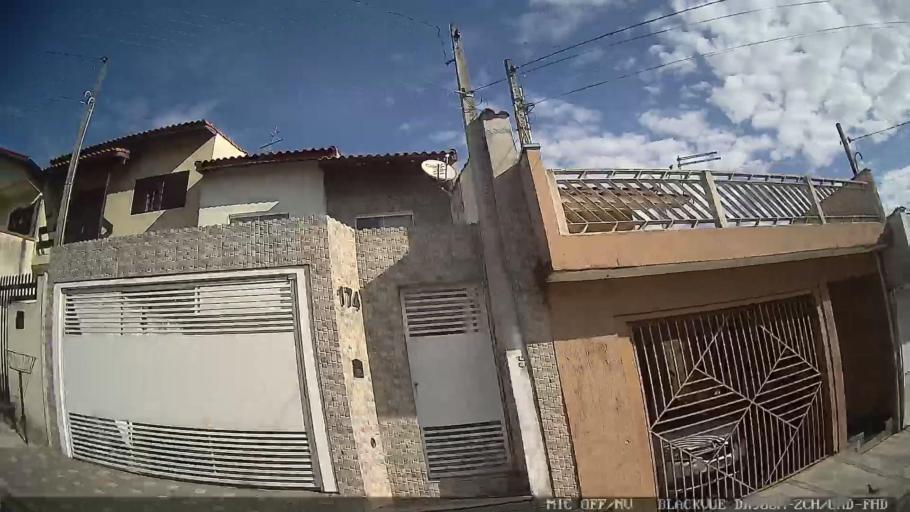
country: BR
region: Sao Paulo
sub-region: Mogi das Cruzes
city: Mogi das Cruzes
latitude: -23.5377
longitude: -46.1777
